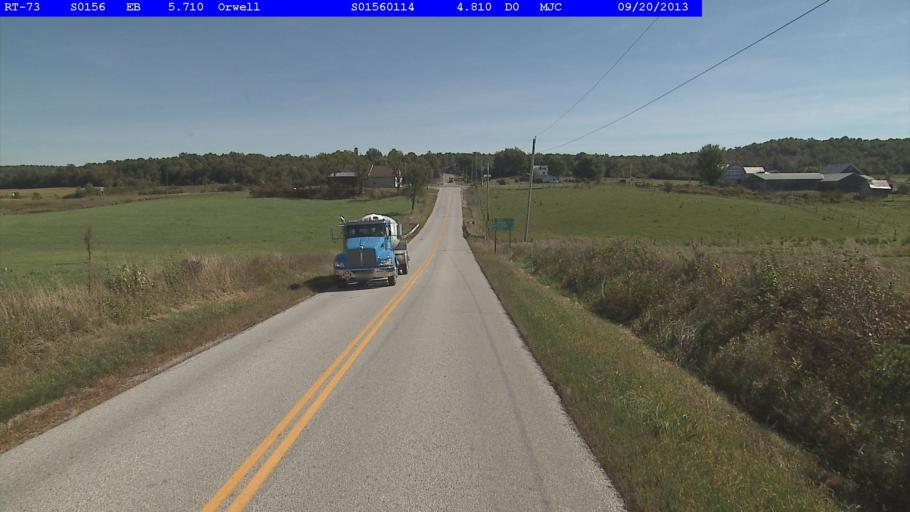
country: US
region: New York
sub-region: Essex County
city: Ticonderoga
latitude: 43.8038
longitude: -73.3077
